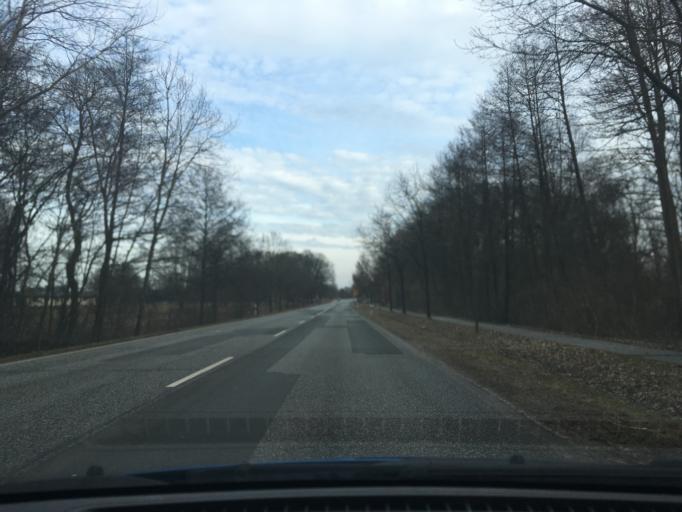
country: DE
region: Mecklenburg-Vorpommern
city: Boizenburg
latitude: 53.3889
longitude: 10.7440
